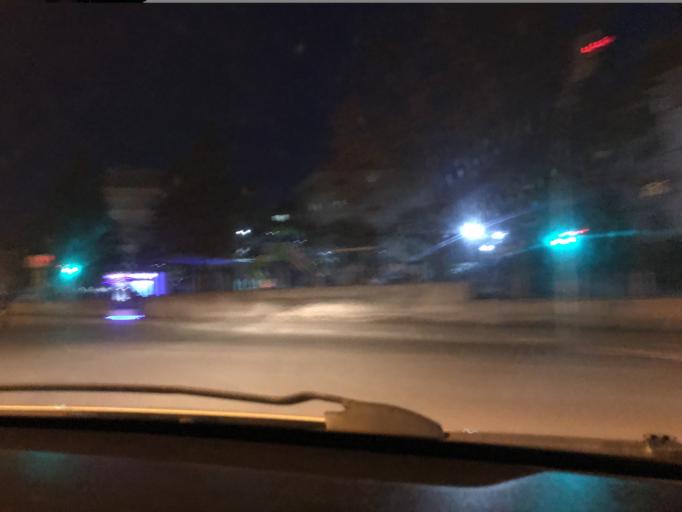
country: TR
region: Ankara
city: Batikent
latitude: 39.9581
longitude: 32.7288
